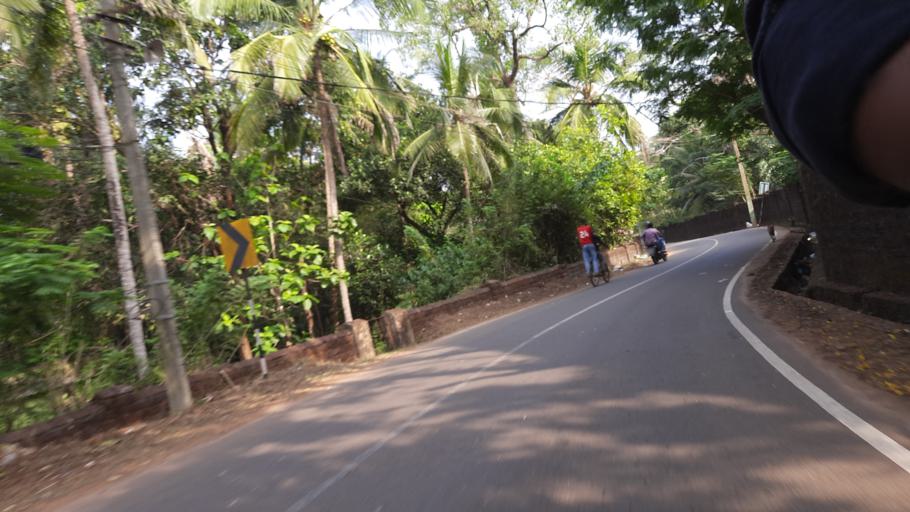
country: IN
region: Kerala
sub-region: Kozhikode
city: Ferokh
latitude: 11.1999
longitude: 75.8572
